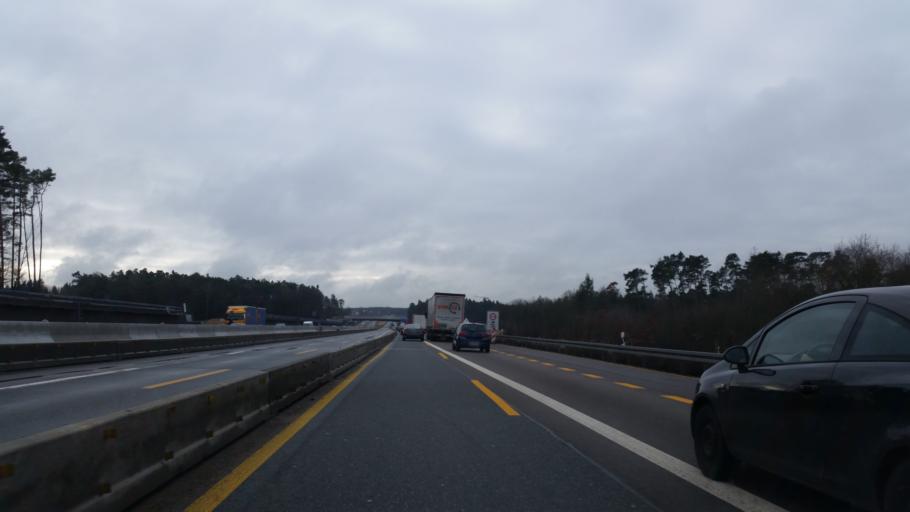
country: DE
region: Bavaria
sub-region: Regierungsbezirk Mittelfranken
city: Schwabach
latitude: 49.3317
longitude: 11.0583
